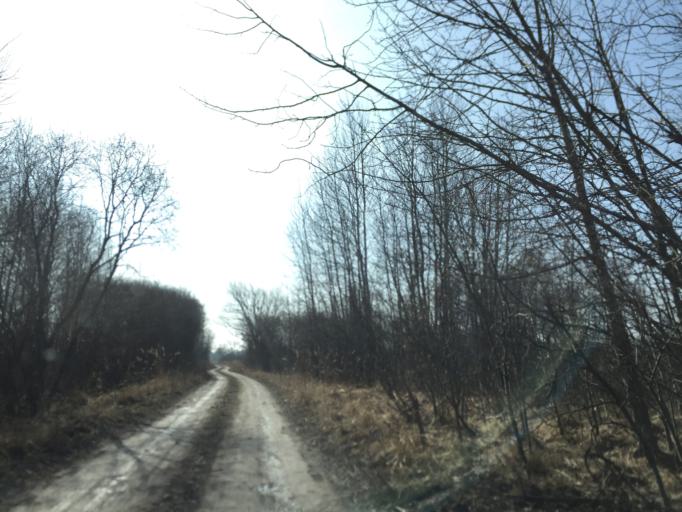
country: LV
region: Dundaga
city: Dundaga
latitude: 57.9314
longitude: 22.0638
